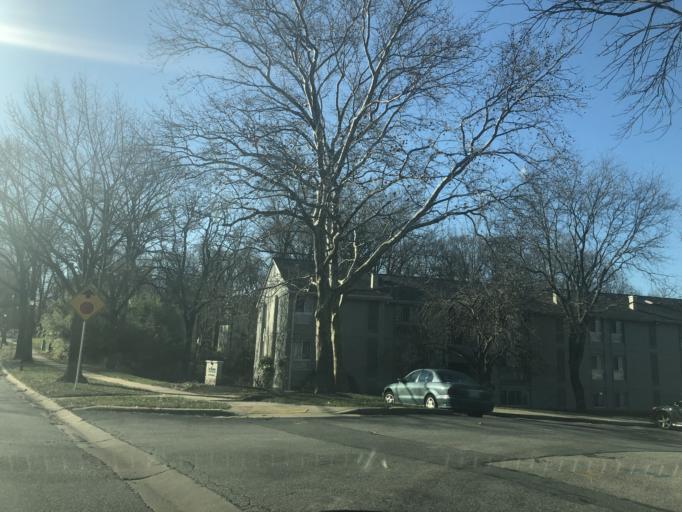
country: US
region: Maryland
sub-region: Howard County
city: Columbia
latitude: 39.2093
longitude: -76.8479
